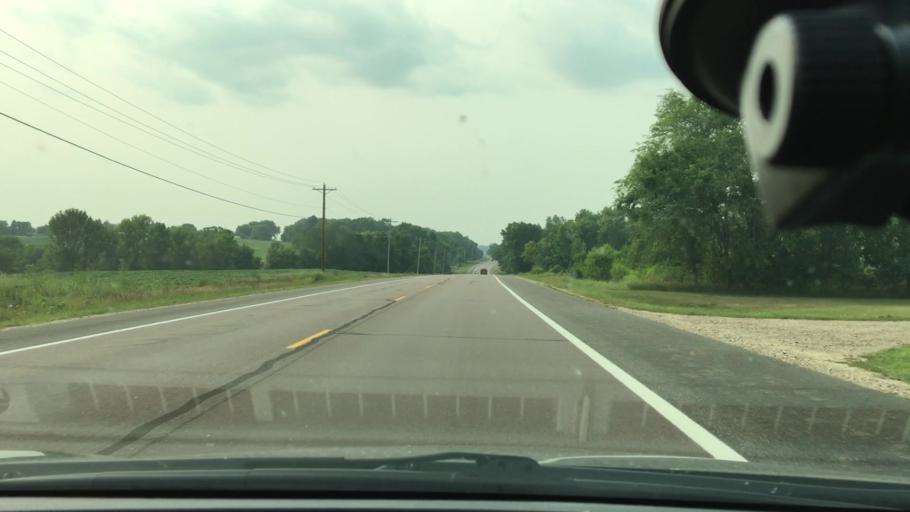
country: US
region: Minnesota
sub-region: Hennepin County
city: Dayton
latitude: 45.2475
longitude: -93.5329
